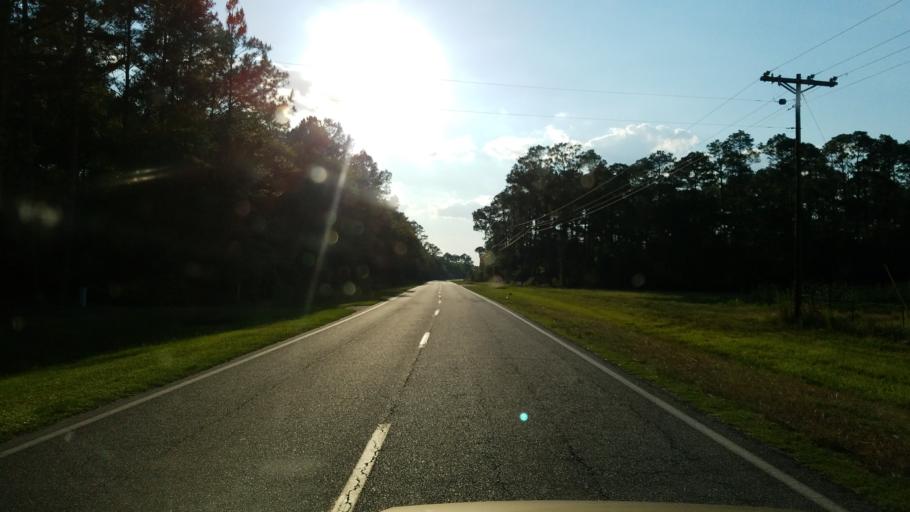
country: US
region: Georgia
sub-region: Berrien County
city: Nashville
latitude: 31.1951
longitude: -83.2159
